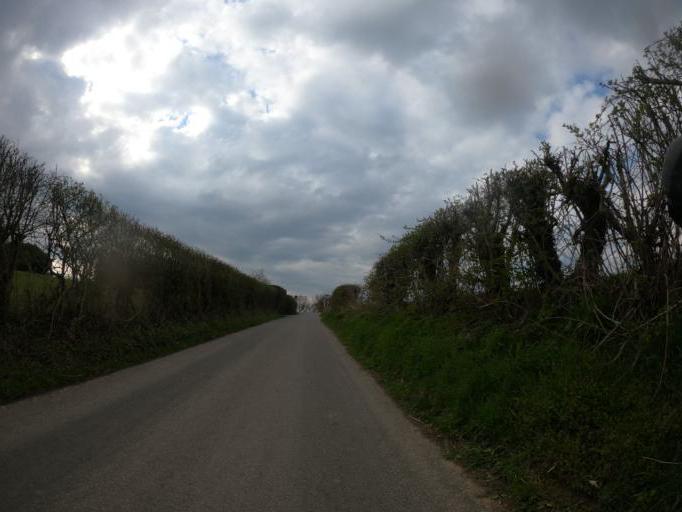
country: BE
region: Wallonia
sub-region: Province de Liege
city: Raeren
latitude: 50.7335
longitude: 6.1460
